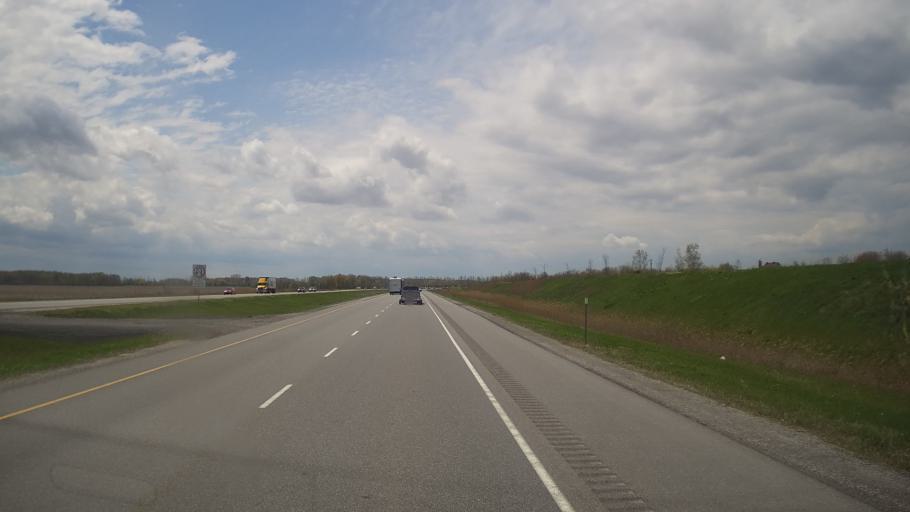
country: CA
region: Quebec
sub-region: Monteregie
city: Beauharnois
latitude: 45.3273
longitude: -73.8138
